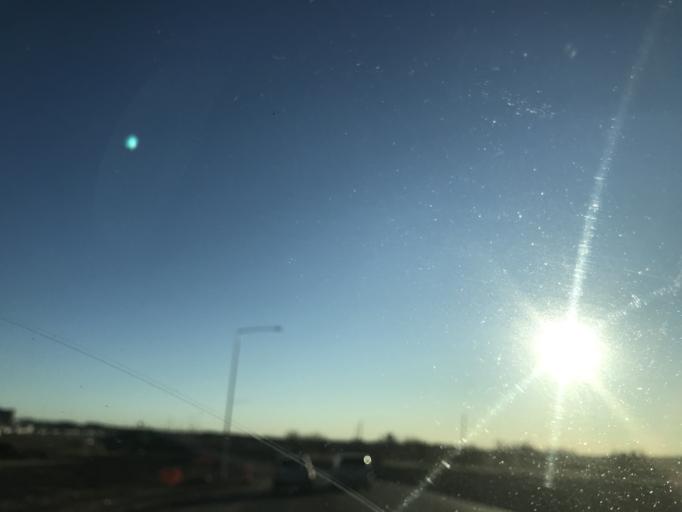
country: US
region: Colorado
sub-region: Adams County
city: Commerce City
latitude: 39.7772
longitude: -104.8947
